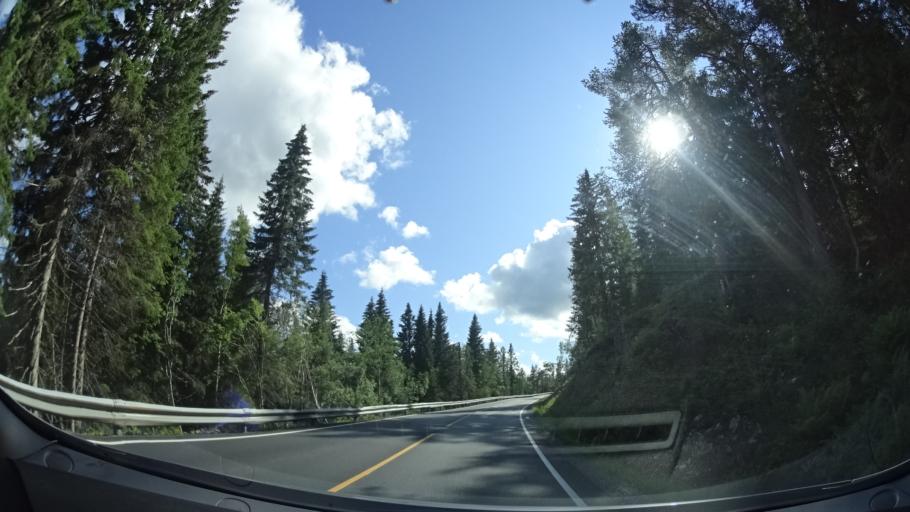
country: NO
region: Sor-Trondelag
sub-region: Snillfjord
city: Krokstadora
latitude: 63.2307
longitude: 9.5776
